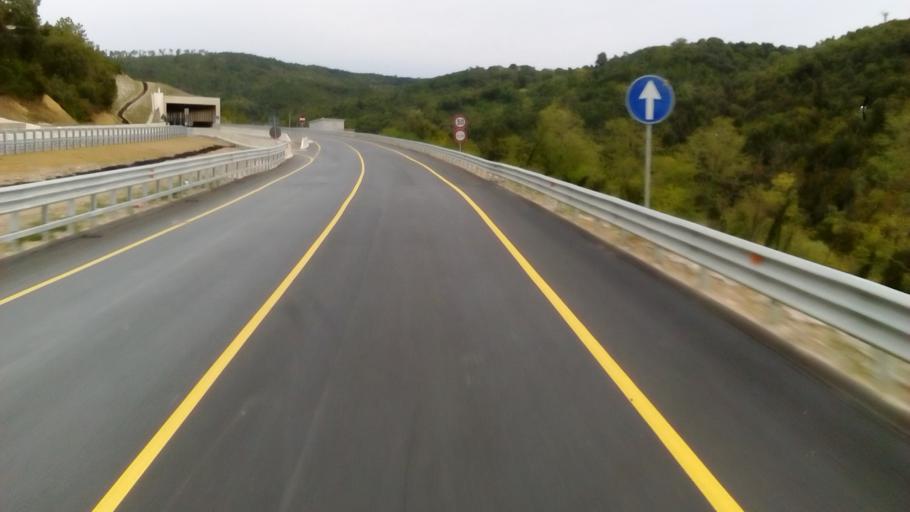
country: IT
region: Tuscany
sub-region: Provincia di Grosseto
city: Civitella Marittima
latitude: 43.0442
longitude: 11.2859
